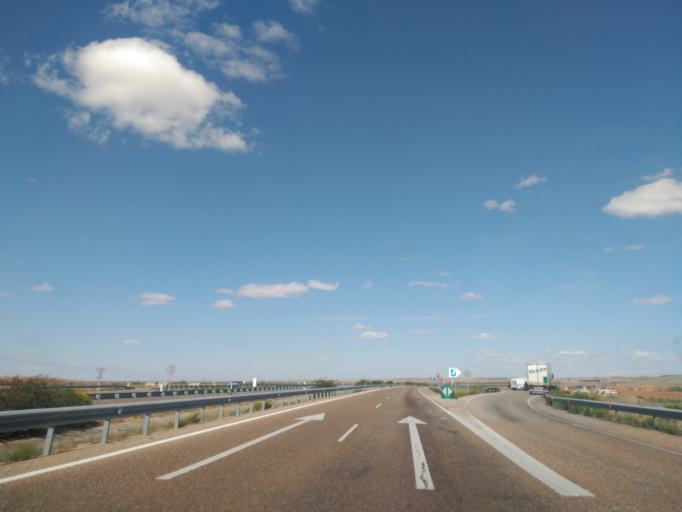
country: ES
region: Castille and Leon
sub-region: Provincia de Valladolid
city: Siete Iglesias de Trabancos
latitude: 41.3599
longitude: -5.1677
